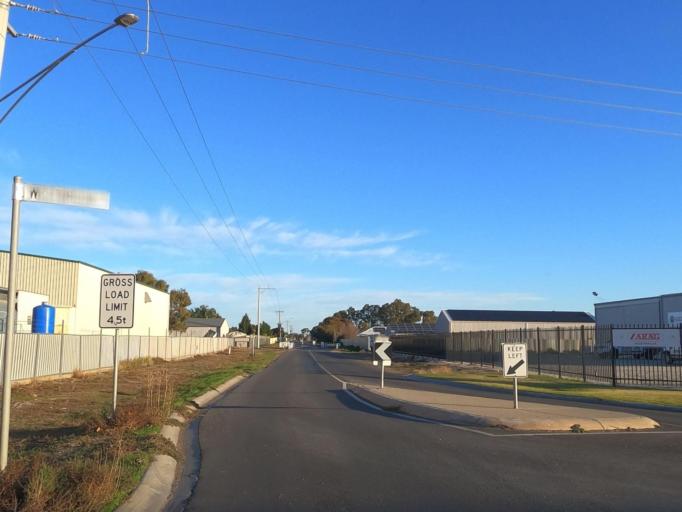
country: AU
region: Victoria
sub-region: Swan Hill
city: Swan Hill
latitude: -35.3281
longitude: 143.5349
